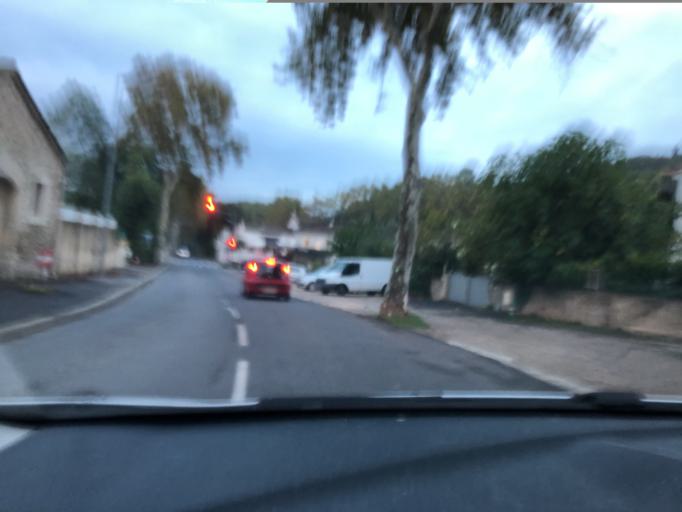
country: FR
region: Languedoc-Roussillon
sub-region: Departement de l'Herault
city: Montferrier-sur-Lez
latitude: 43.6700
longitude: 3.8617
